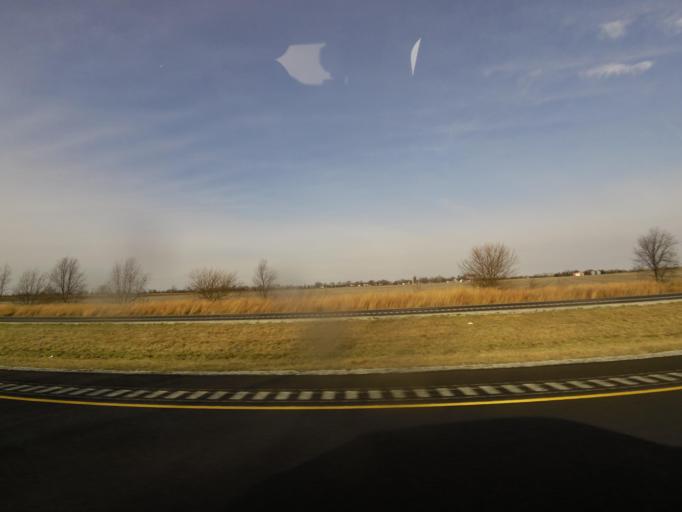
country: US
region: Illinois
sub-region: Macon County
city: Macon
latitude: 39.7685
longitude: -88.9730
